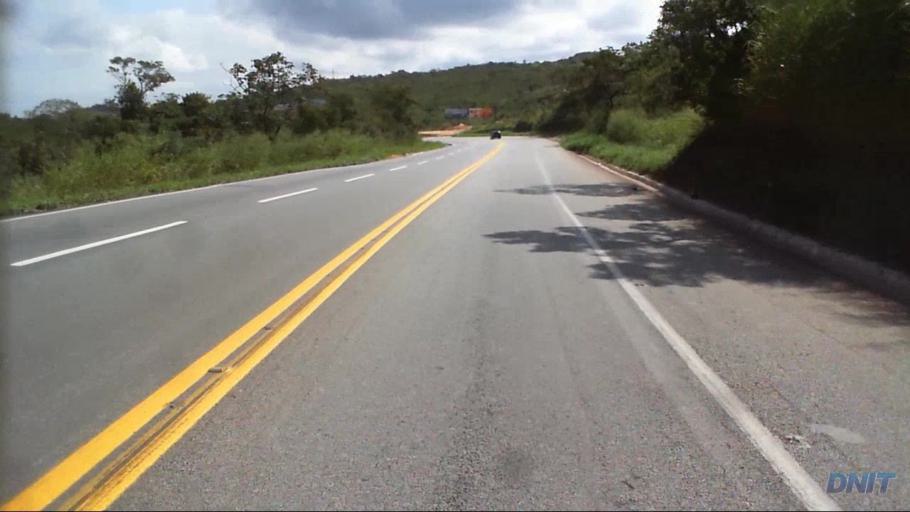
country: BR
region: Minas Gerais
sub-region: Santa Luzia
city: Santa Luzia
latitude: -19.8090
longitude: -43.7817
